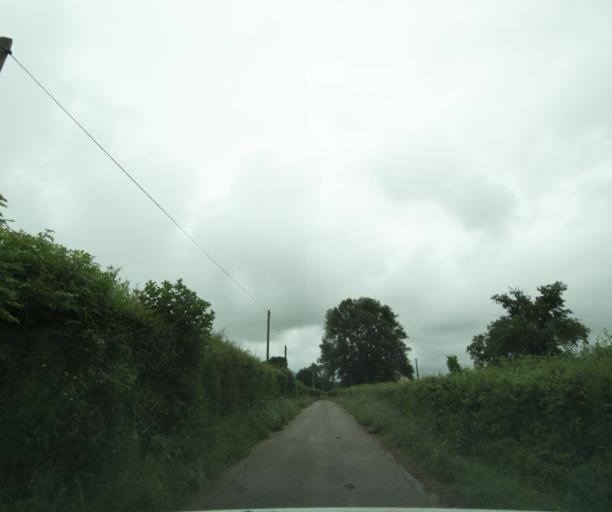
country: FR
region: Bourgogne
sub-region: Departement de Saone-et-Loire
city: Charolles
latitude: 46.4567
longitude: 4.3202
